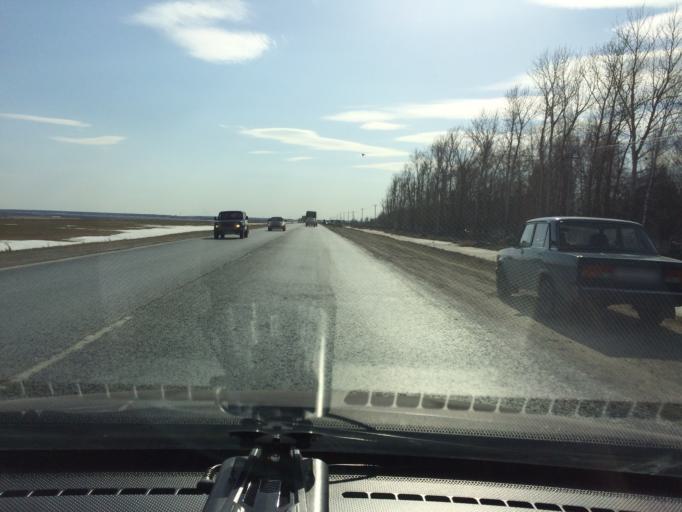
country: RU
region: Mariy-El
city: Yoshkar-Ola
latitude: 56.7027
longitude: 48.0713
